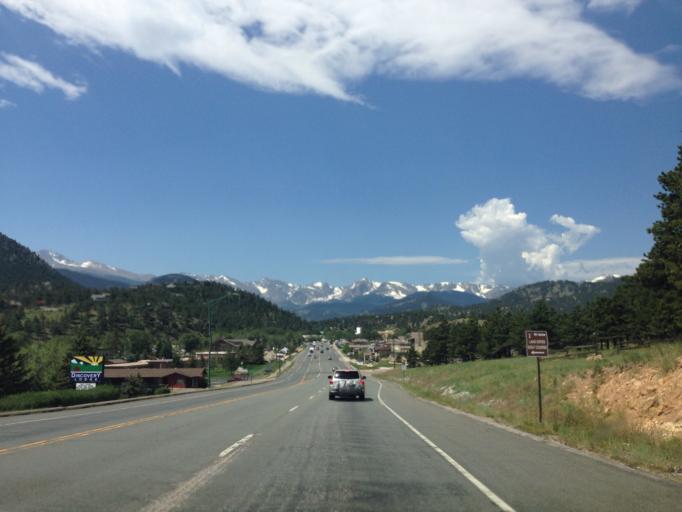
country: US
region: Colorado
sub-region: Larimer County
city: Estes Park
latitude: 40.3815
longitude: -105.5103
